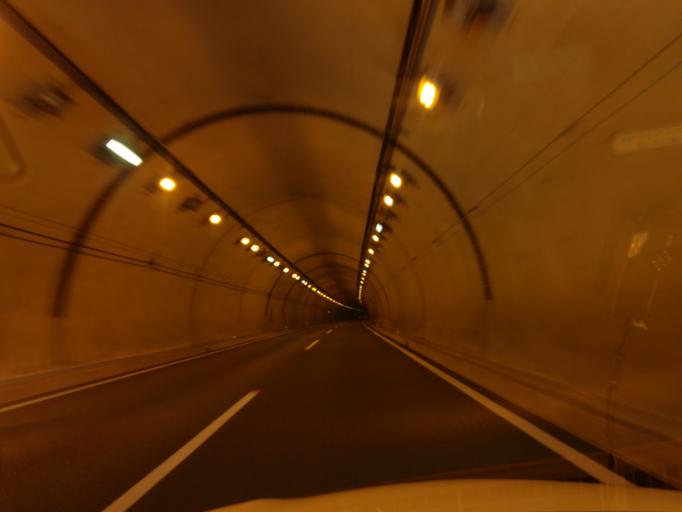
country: JP
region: Ehime
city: Kawanoecho
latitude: 33.8365
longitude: 133.6546
